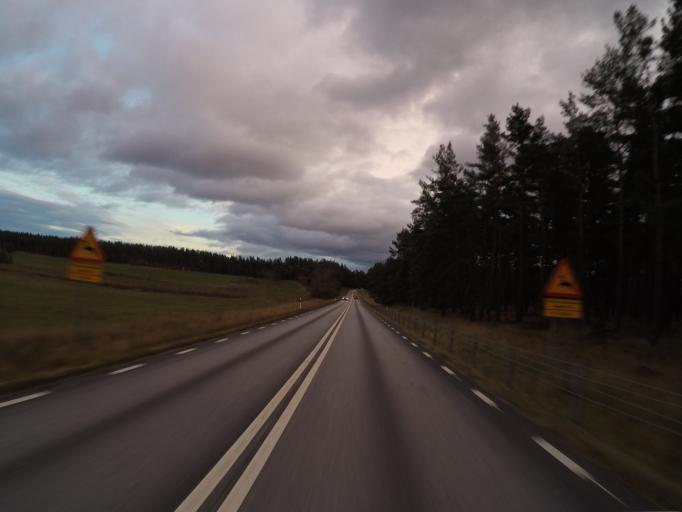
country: SE
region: Skane
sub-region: Kristianstads Kommun
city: Degeberga
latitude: 55.8784
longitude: 14.0871
